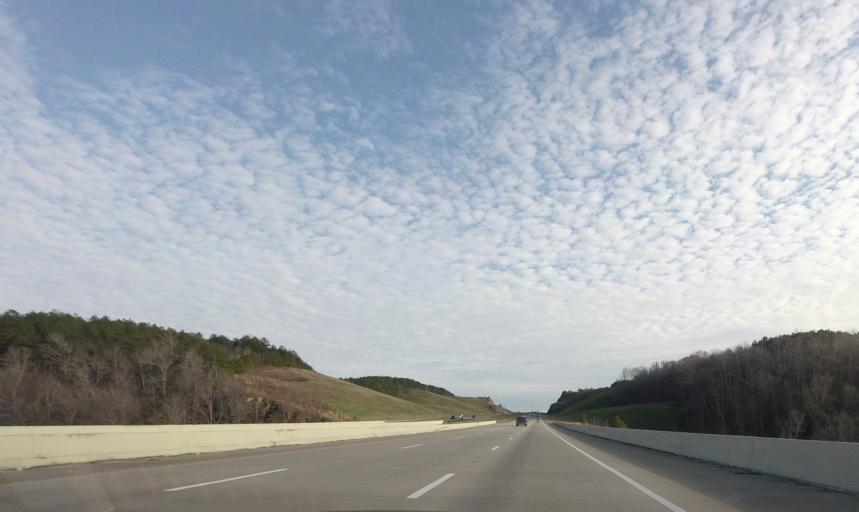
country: US
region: Alabama
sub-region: Walker County
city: Dora
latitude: 33.7076
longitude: -87.1430
